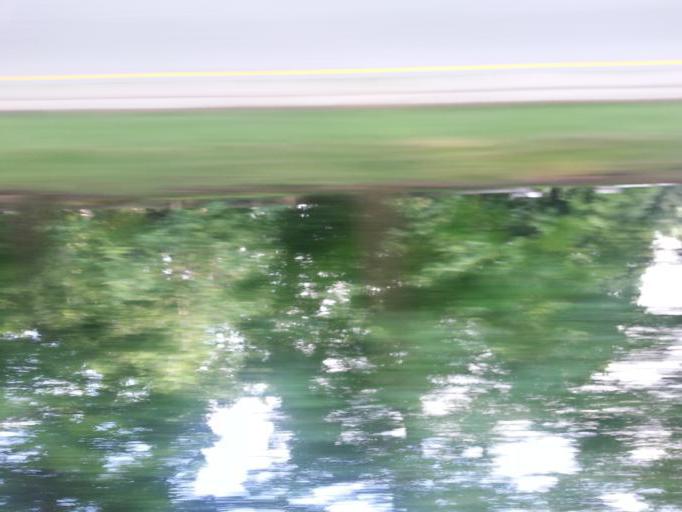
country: US
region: Kentucky
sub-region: Fayette County
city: Lexington-Fayette
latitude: 38.0832
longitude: -84.4436
